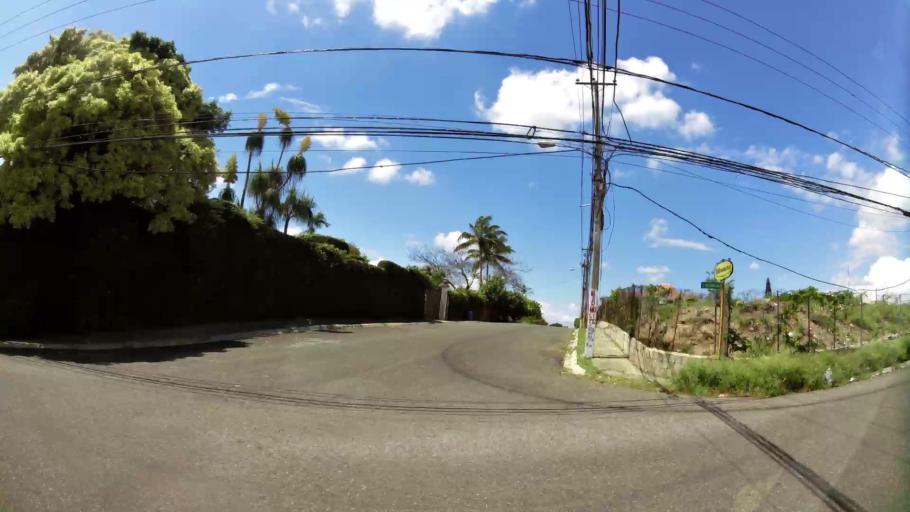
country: DO
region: Santiago
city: Santiago de los Caballeros
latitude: 19.4660
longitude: -70.6777
